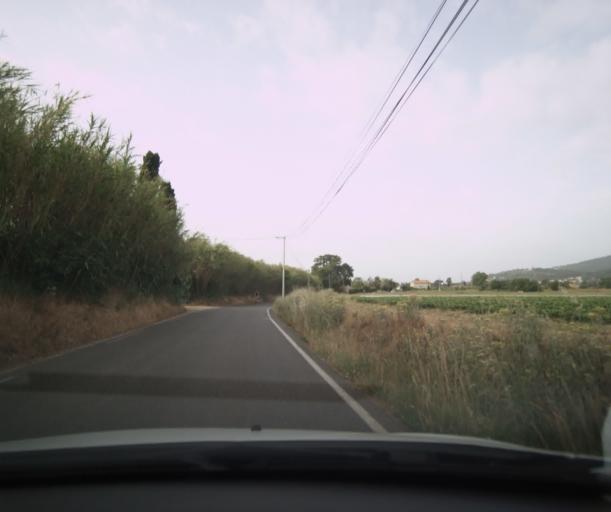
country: FR
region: Provence-Alpes-Cote d'Azur
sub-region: Departement du Var
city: Hyeres
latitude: 43.1138
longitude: 6.1449
